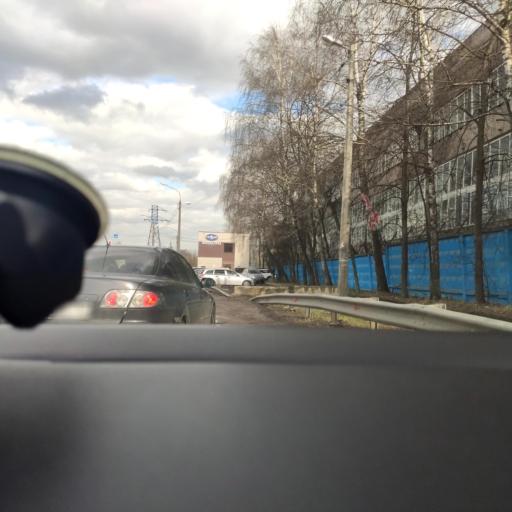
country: RU
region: Moskovskaya
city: Chornaya
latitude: 55.7505
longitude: 38.0534
